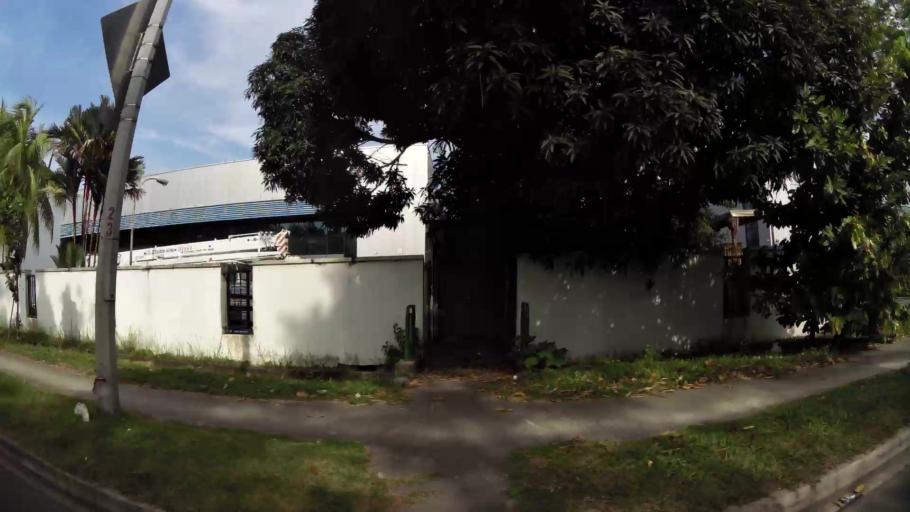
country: MY
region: Johor
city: Johor Bahru
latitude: 1.3282
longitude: 103.6393
